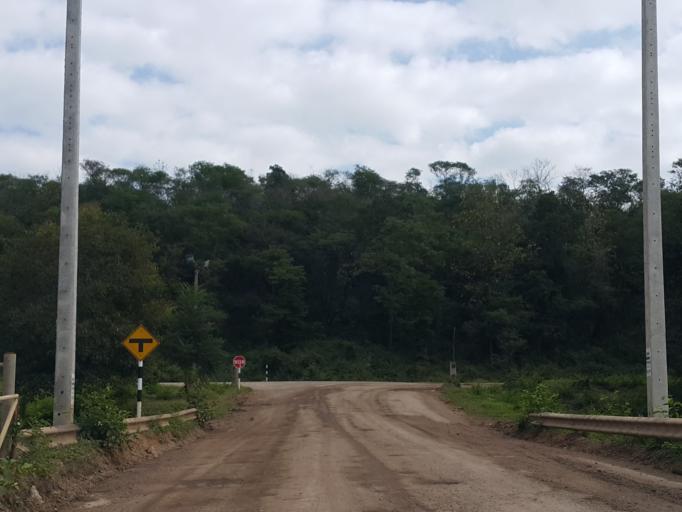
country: TH
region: Lampang
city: Mae Mo
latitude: 18.3162
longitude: 99.7465
